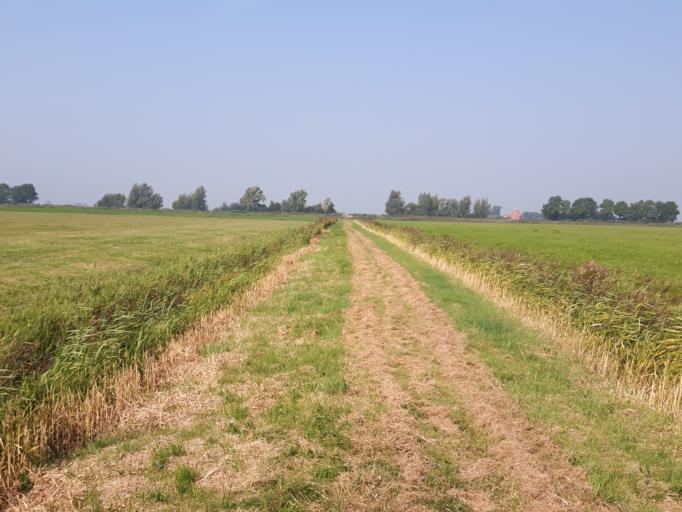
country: NL
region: Friesland
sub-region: Sudwest Fryslan
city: Bolsward
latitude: 53.0322
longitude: 5.4959
